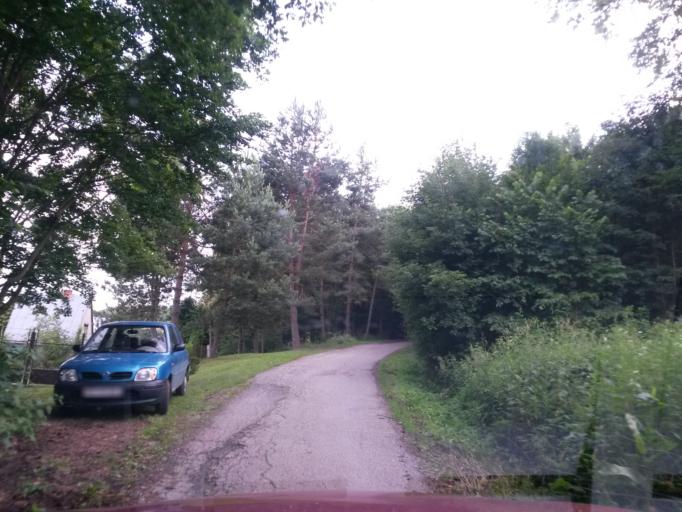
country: SK
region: Presovsky
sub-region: Okres Presov
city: Presov
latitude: 48.9830
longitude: 21.1725
